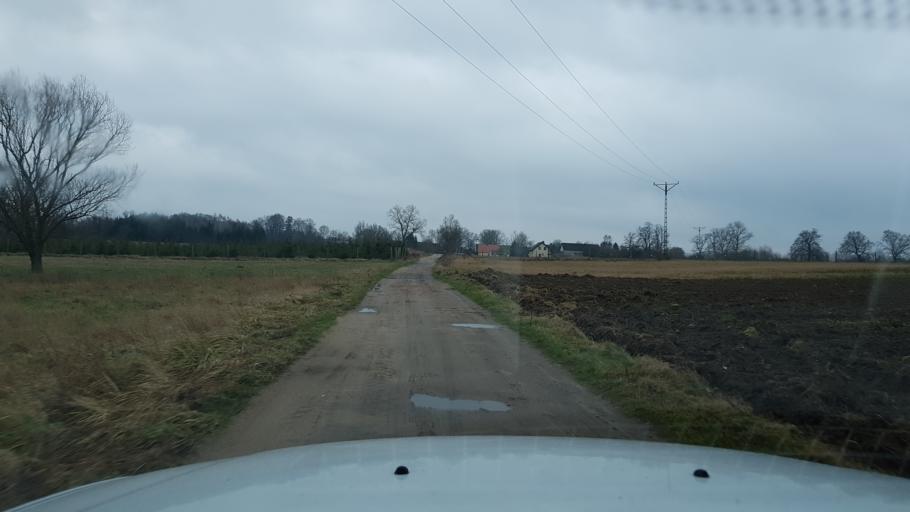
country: PL
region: West Pomeranian Voivodeship
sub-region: Powiat gryficki
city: Brojce
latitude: 53.9720
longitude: 15.3008
